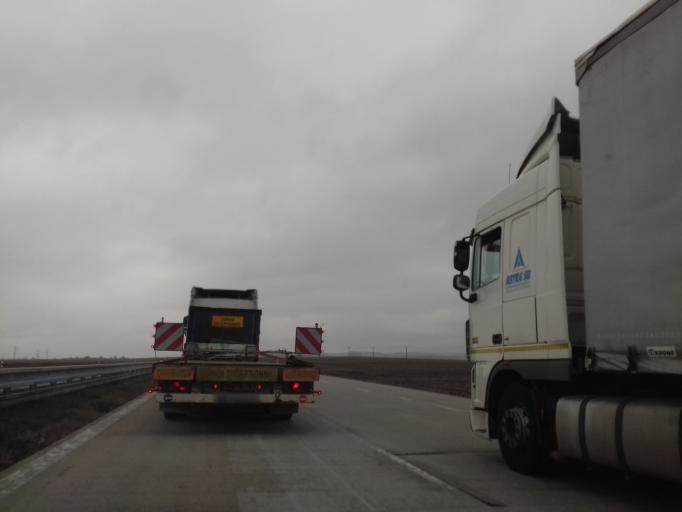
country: CZ
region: South Moravian
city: Rakvice
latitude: 48.8691
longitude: 16.8266
